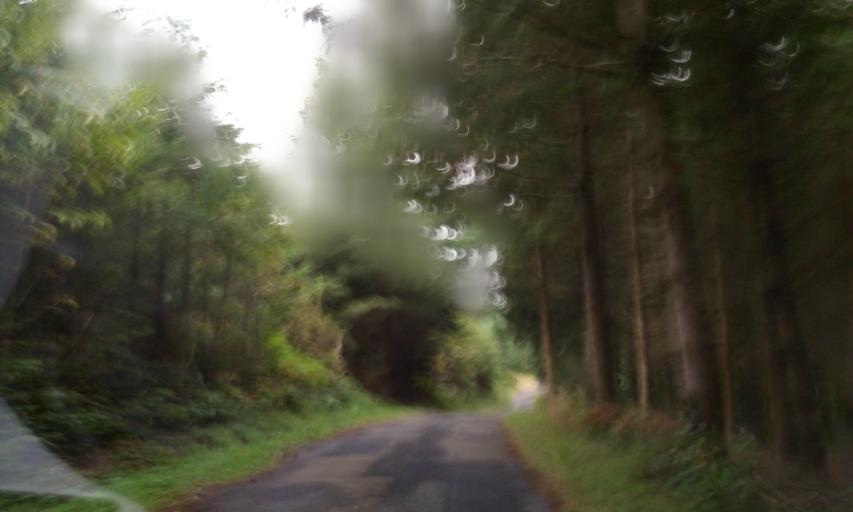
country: FR
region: Rhone-Alpes
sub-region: Departement du Rhone
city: Cublize
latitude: 45.9995
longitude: 4.4176
